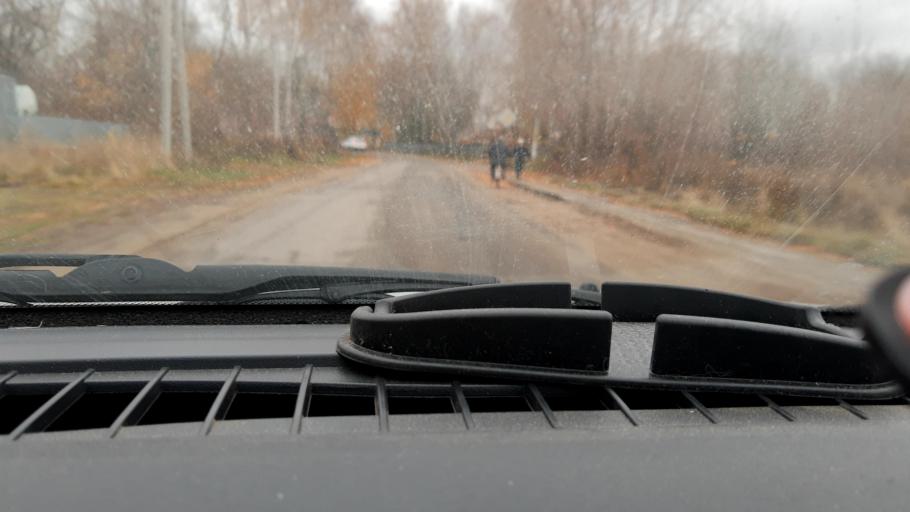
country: RU
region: Nizjnij Novgorod
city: Neklyudovo
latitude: 56.4093
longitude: 44.0329
